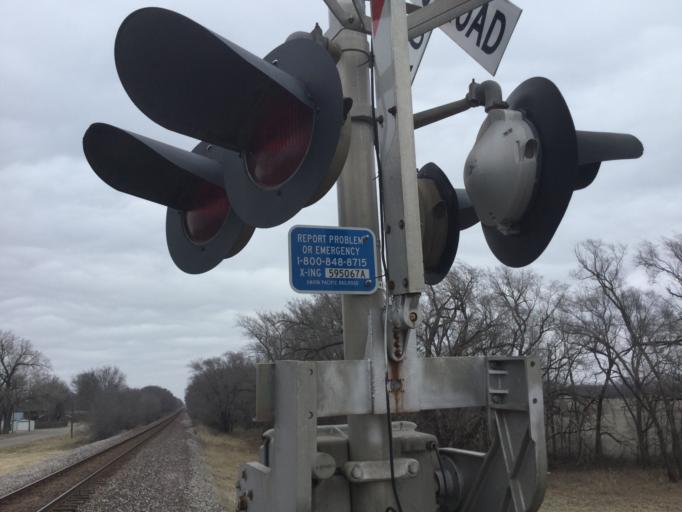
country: US
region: Kansas
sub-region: Sedgwick County
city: Haysville
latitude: 37.5790
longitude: -97.3477
